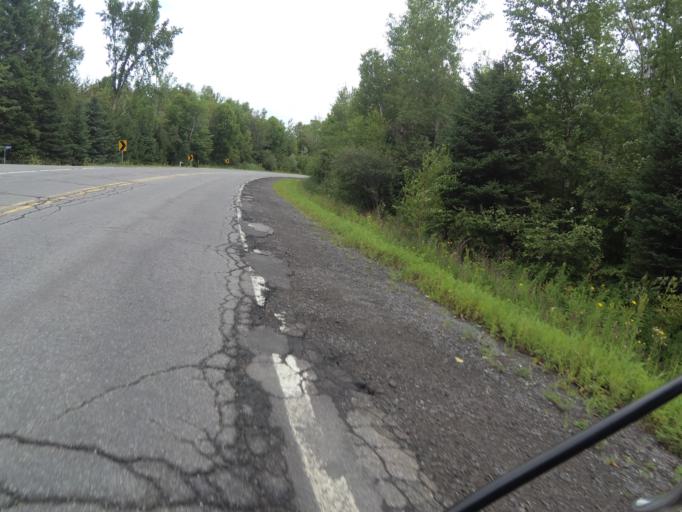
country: CA
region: Ontario
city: Bourget
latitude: 45.3538
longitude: -75.2765
